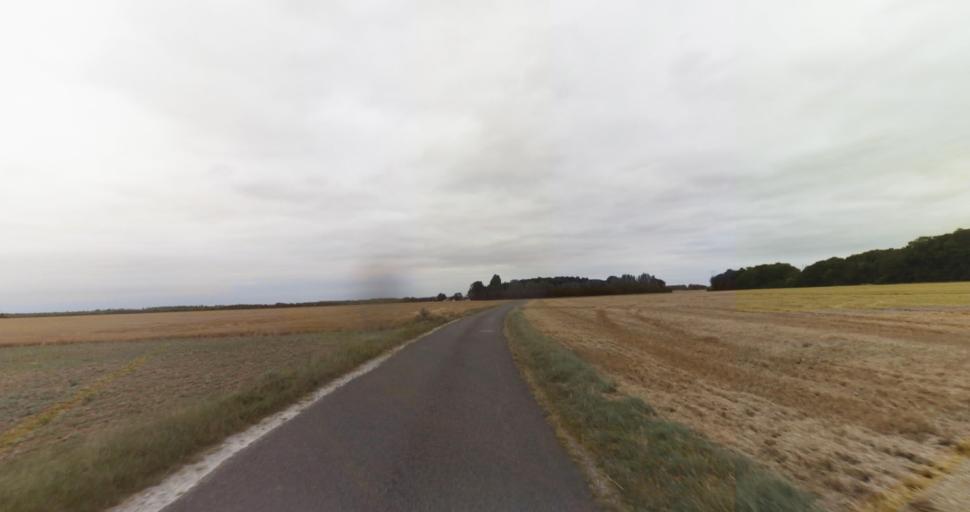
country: FR
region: Haute-Normandie
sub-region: Departement de l'Eure
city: Marcilly-sur-Eure
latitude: 48.8652
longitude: 1.2636
